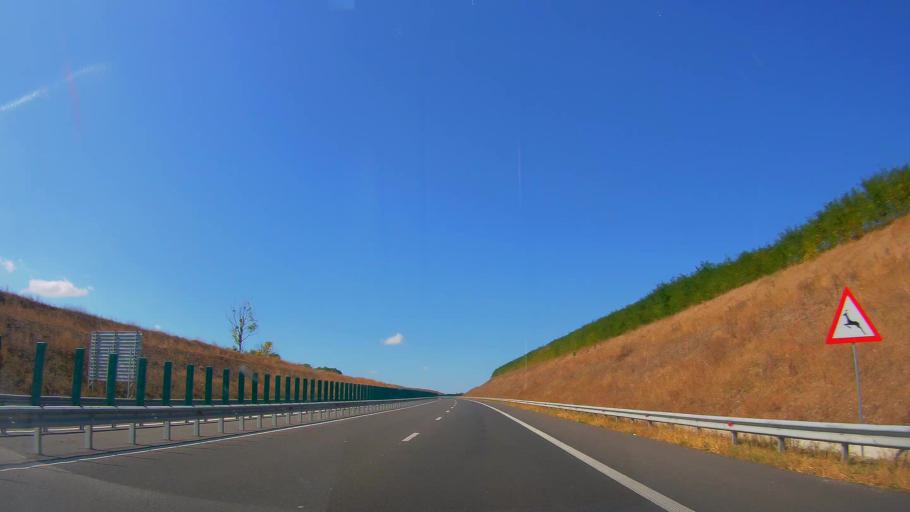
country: RO
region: Cluj
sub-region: Comuna Gilau
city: Gilau
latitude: 46.7617
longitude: 23.3942
